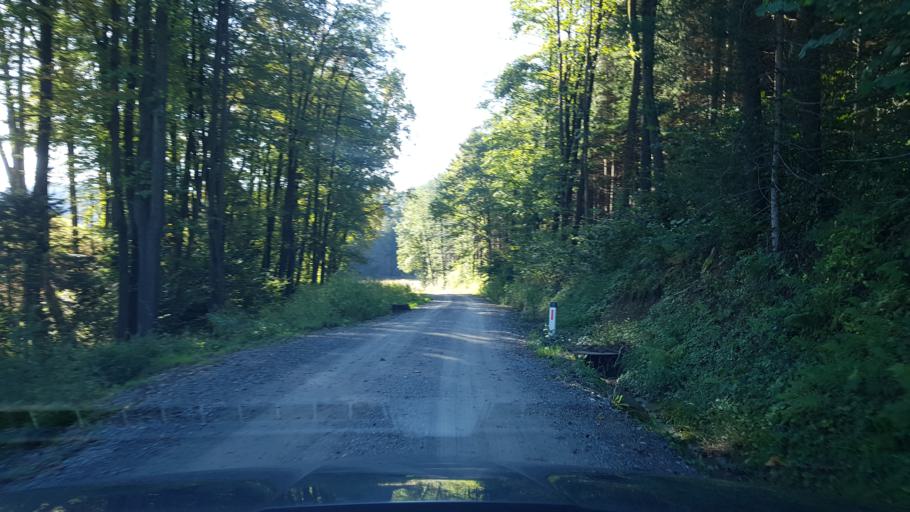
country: AT
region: Styria
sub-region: Politischer Bezirk Deutschlandsberg
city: Sankt Martin im Sulmtal
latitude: 46.7381
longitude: 15.3097
